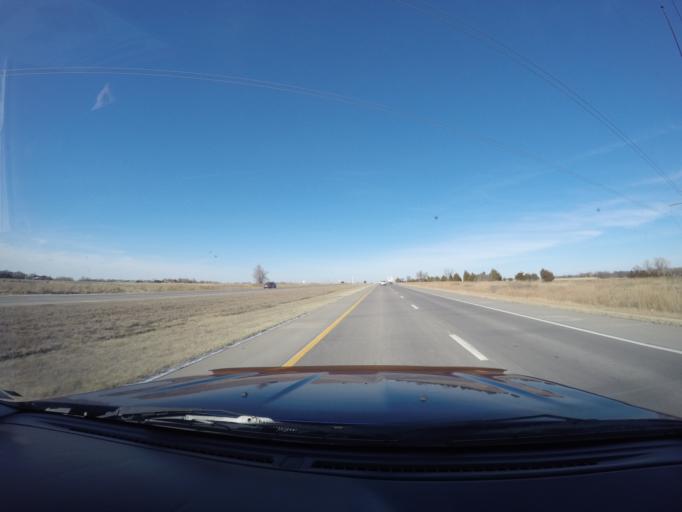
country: US
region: Kansas
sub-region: Harvey County
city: Sedgwick
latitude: 37.9219
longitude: -97.3273
